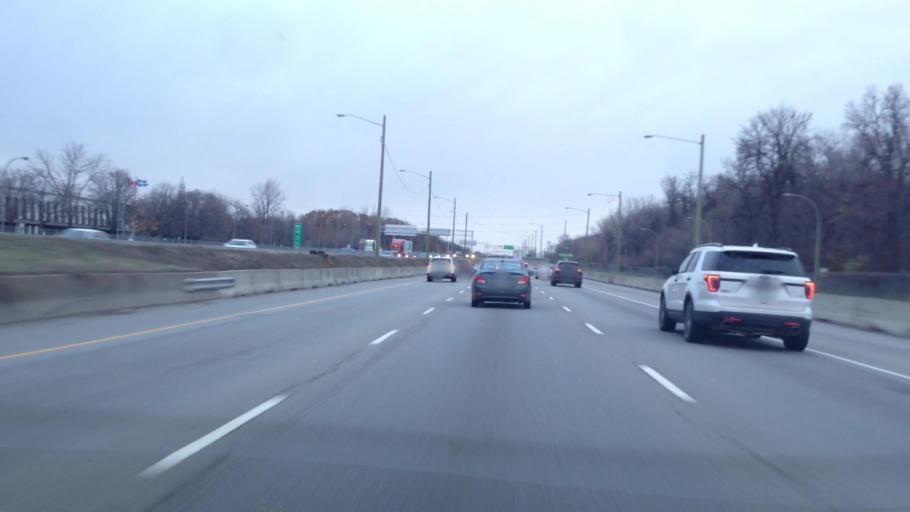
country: CA
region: Quebec
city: Baie-D'Urfe
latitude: 45.4217
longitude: -73.9273
